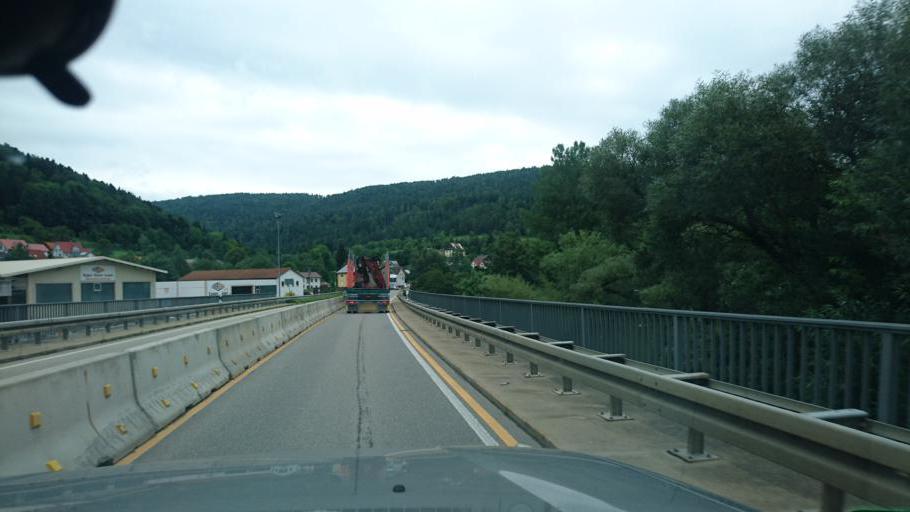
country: DE
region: Baden-Wuerttemberg
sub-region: Freiburg Region
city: Sulz am Neckar
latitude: 48.4189
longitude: 8.6364
